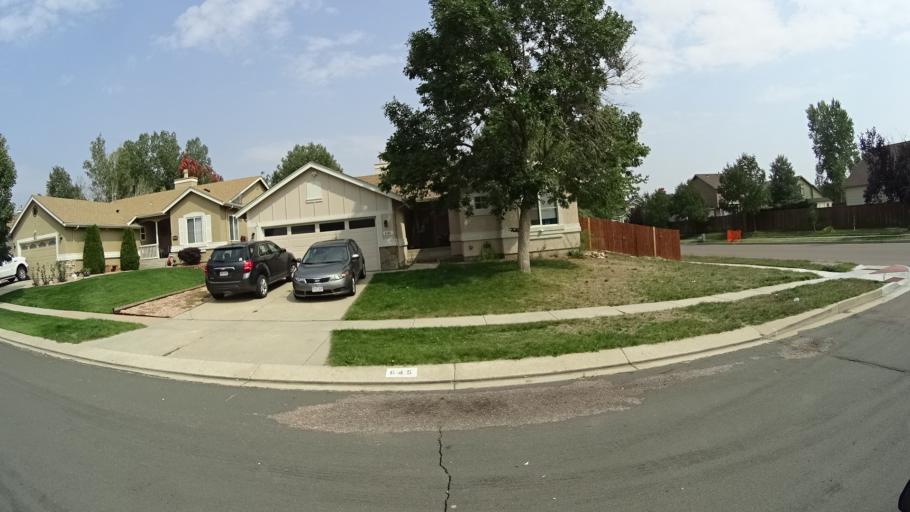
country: US
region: Colorado
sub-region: El Paso County
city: Cimarron Hills
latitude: 38.8223
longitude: -104.7376
